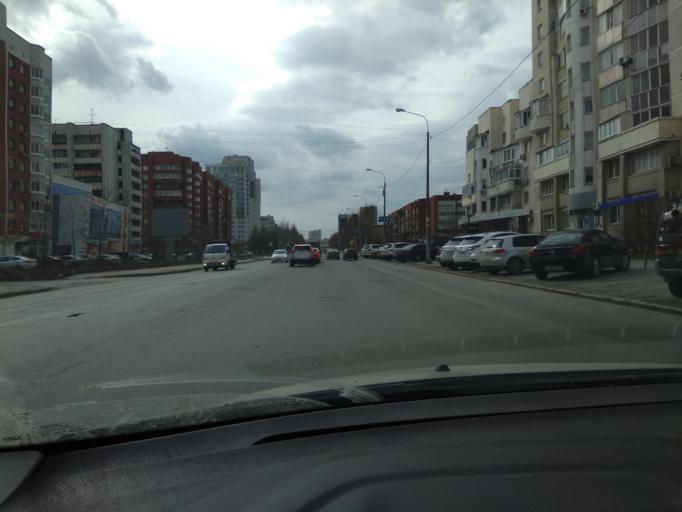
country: RU
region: Sverdlovsk
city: Yekaterinburg
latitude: 56.8152
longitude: 60.6018
